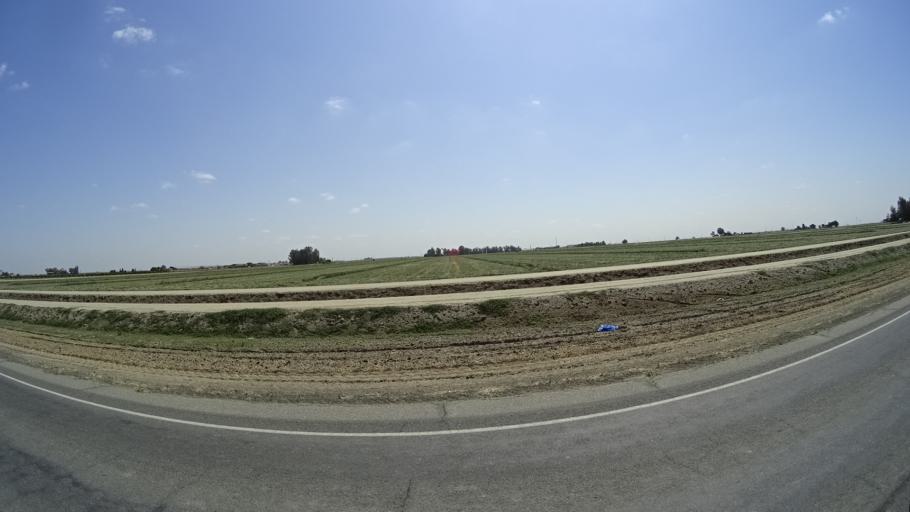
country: US
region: California
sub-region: Kings County
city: Home Garden
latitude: 36.2167
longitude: -119.6370
